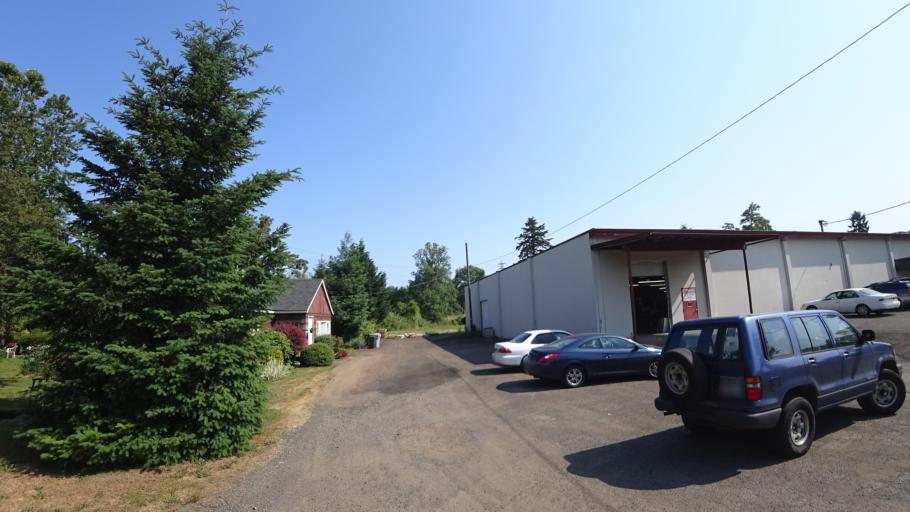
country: US
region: Oregon
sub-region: Multnomah County
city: Lents
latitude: 45.4570
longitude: -122.5893
